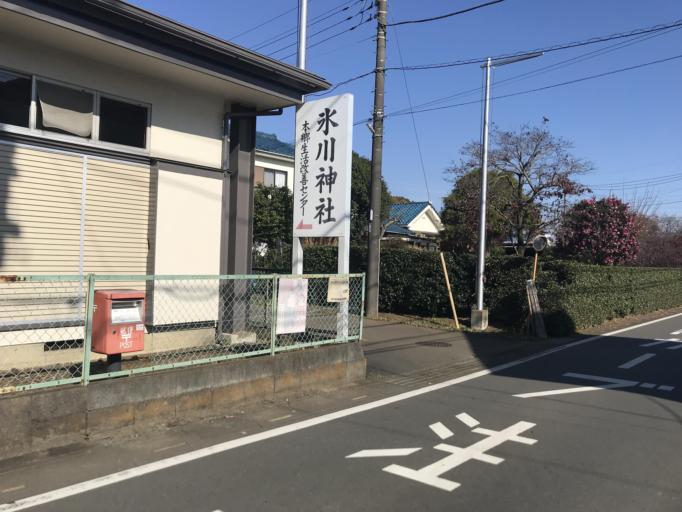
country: JP
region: Saitama
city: Tokorozawa
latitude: 35.7931
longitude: 139.5232
